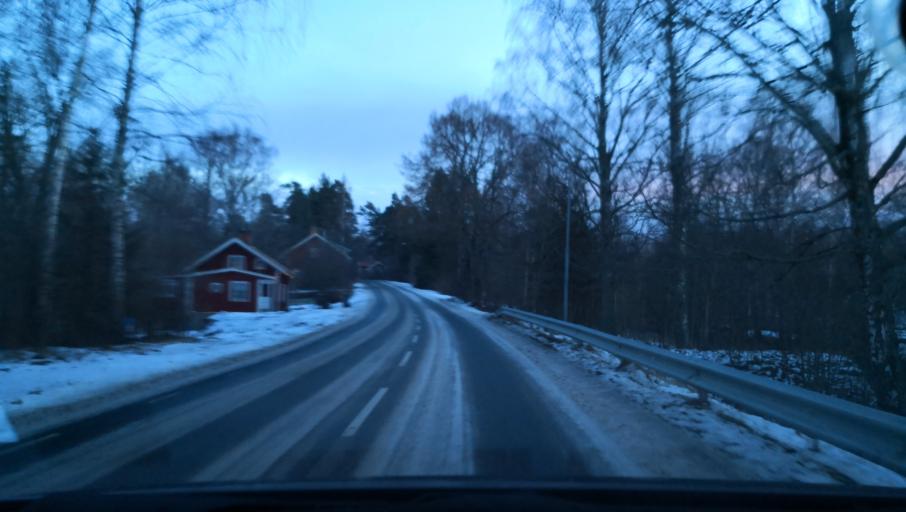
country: SE
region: Soedermanland
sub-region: Katrineholms Kommun
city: Katrineholm
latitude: 59.0865
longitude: 16.2165
